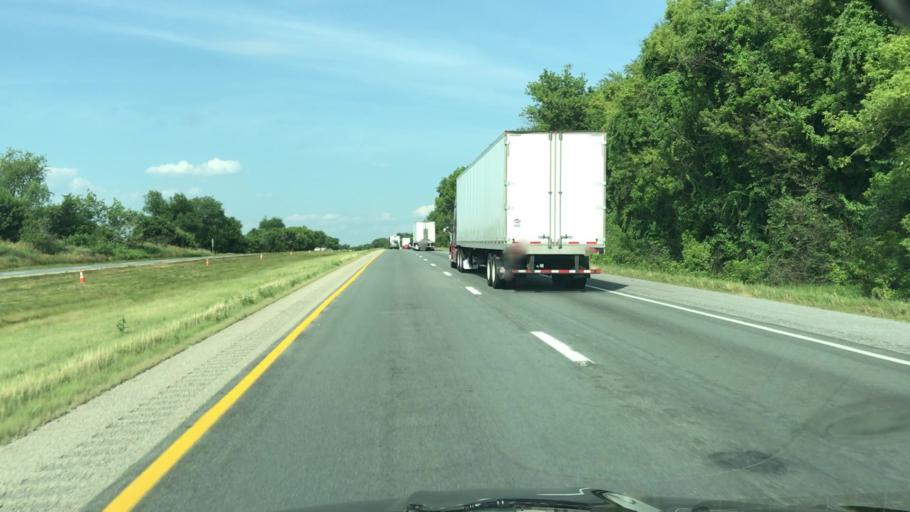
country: US
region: Pennsylvania
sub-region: Cumberland County
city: Newville
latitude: 40.1013
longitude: -77.3945
